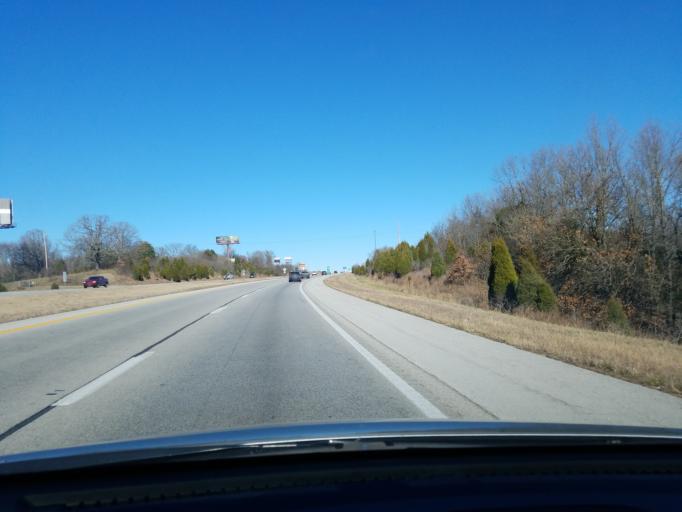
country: US
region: Missouri
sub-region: Taney County
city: Merriam Woods
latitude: 36.7979
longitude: -93.2265
